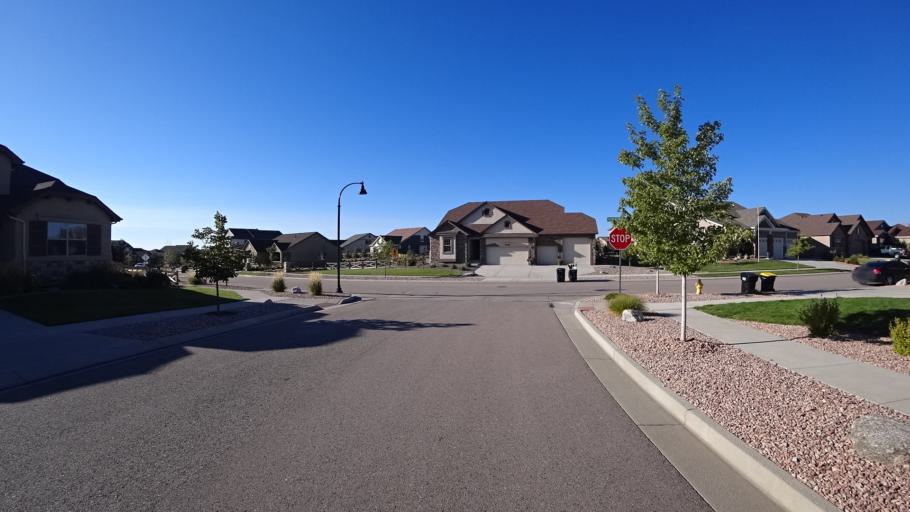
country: US
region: Colorado
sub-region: El Paso County
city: Cimarron Hills
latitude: 38.9361
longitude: -104.6676
